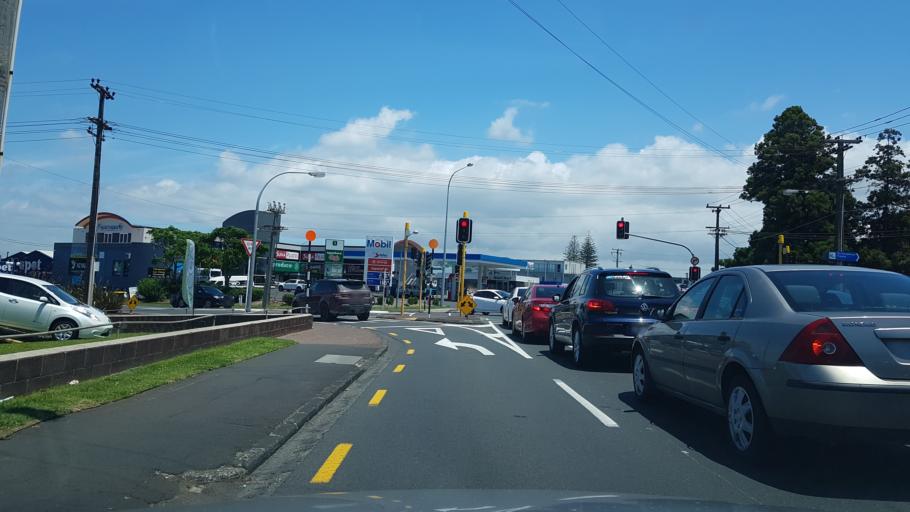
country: NZ
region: Auckland
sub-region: Auckland
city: North Shore
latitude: -36.7898
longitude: 174.7655
